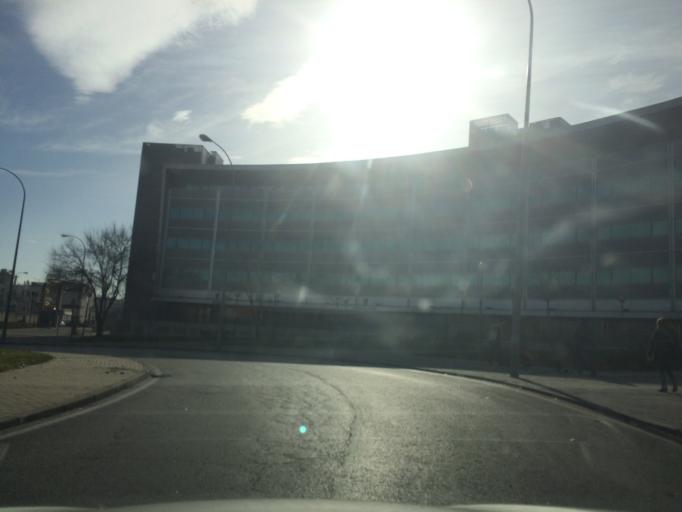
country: ES
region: Madrid
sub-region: Provincia de Madrid
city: Tres Cantos
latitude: 40.5954
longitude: -3.7090
